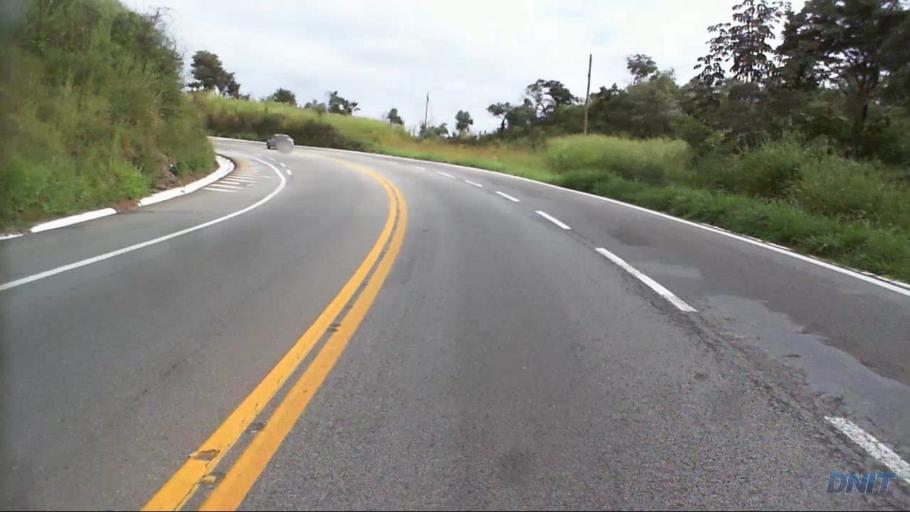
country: BR
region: Minas Gerais
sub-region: Caete
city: Caete
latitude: -19.7379
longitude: -43.6057
